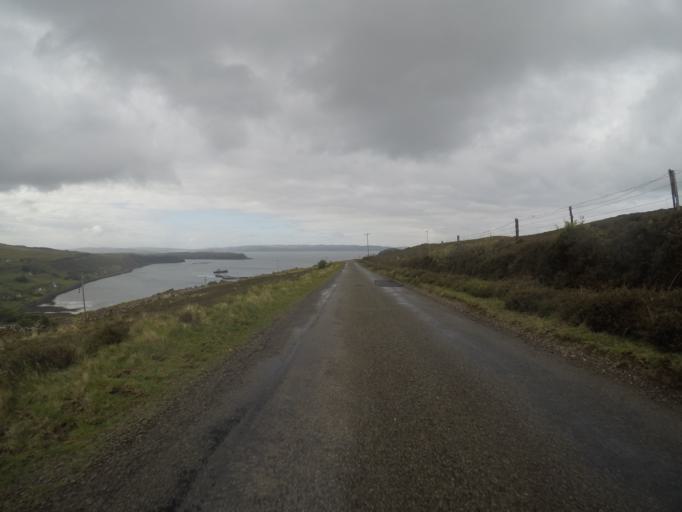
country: GB
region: Scotland
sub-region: Highland
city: Portree
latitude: 57.5952
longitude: -6.3611
